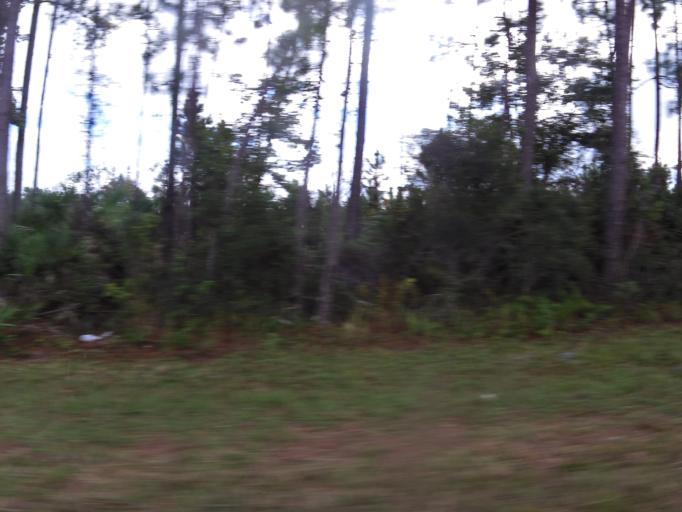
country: US
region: Florida
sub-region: Saint Johns County
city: Villano Beach
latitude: 30.0069
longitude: -81.4058
